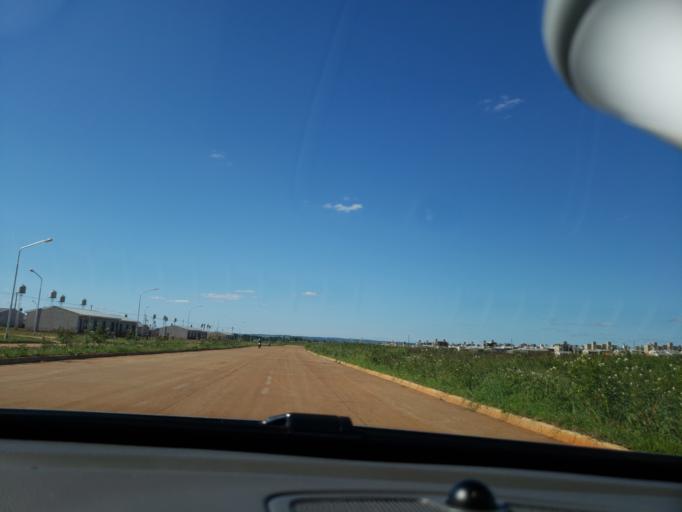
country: AR
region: Misiones
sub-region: Departamento de Capital
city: Posadas
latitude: -27.4063
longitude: -55.9887
